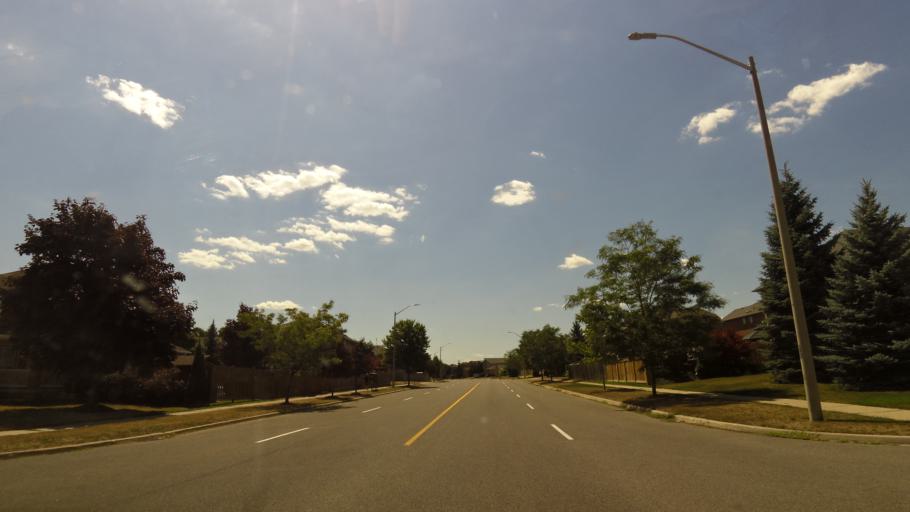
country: CA
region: Ontario
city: Brampton
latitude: 43.6393
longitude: -79.8740
